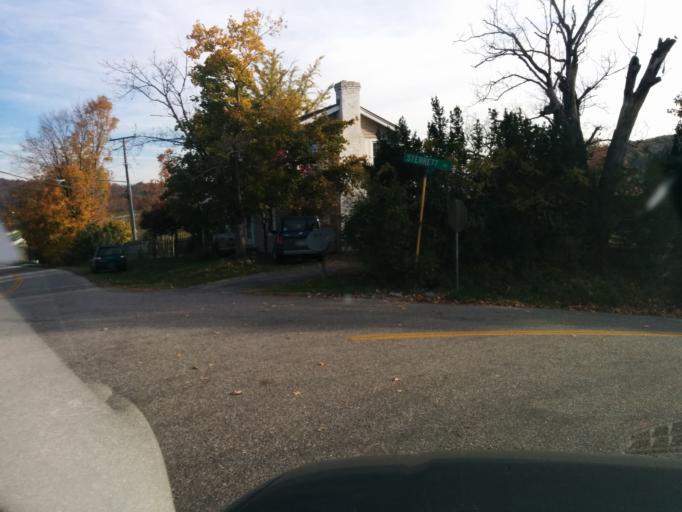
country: US
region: Virginia
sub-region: Rockbridge County
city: East Lexington
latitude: 37.9294
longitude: -79.3187
